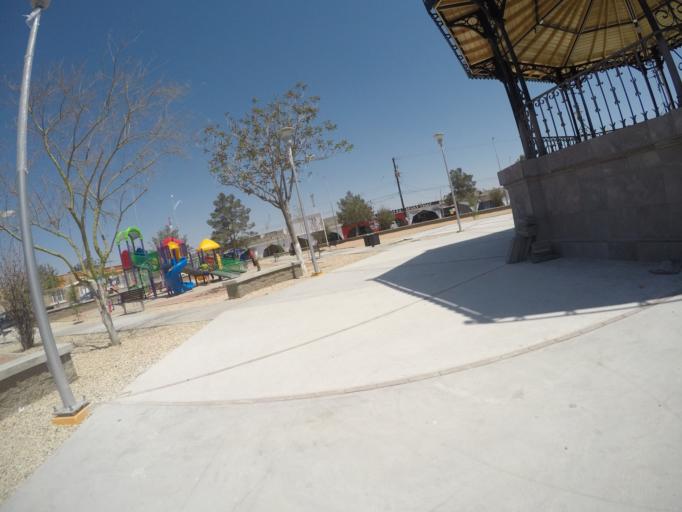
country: MX
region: Chihuahua
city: Ciudad Juarez
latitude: 31.7305
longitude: -106.4822
